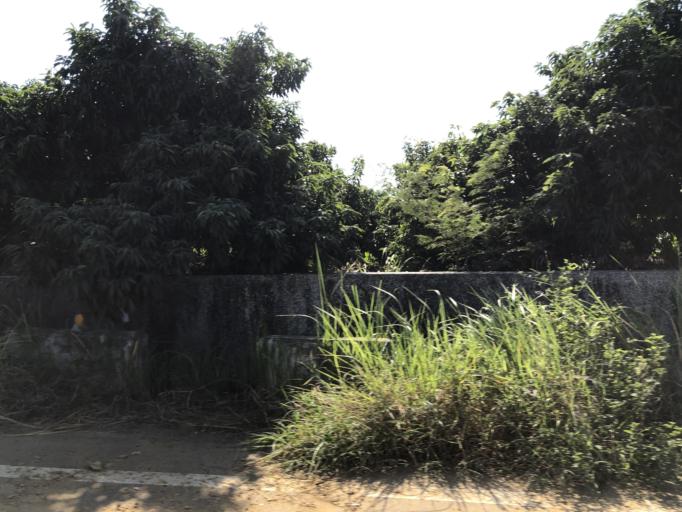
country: TW
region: Taiwan
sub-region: Tainan
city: Tainan
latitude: 23.0385
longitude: 120.3283
